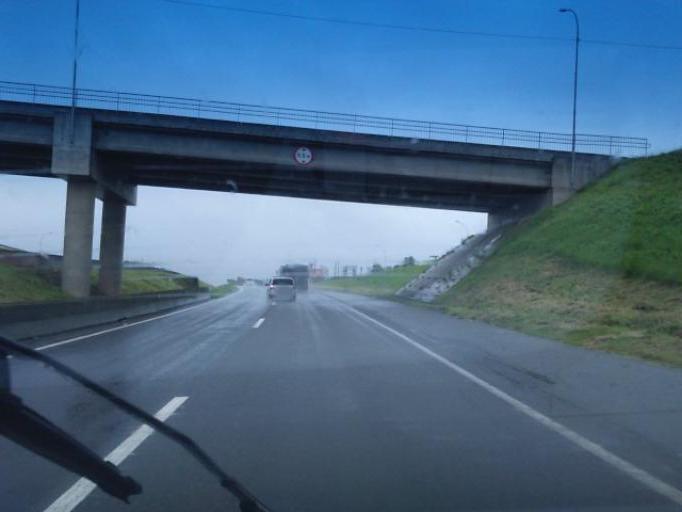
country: BR
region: Sao Paulo
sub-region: Jacupiranga
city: Jacupiranga
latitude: -24.7097
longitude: -48.0188
